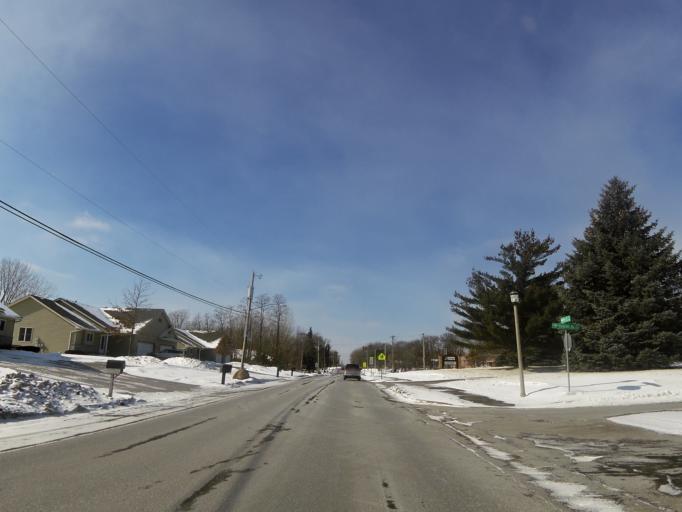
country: US
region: Minnesota
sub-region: Washington County
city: Oakdale
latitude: 44.9706
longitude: -92.9449
